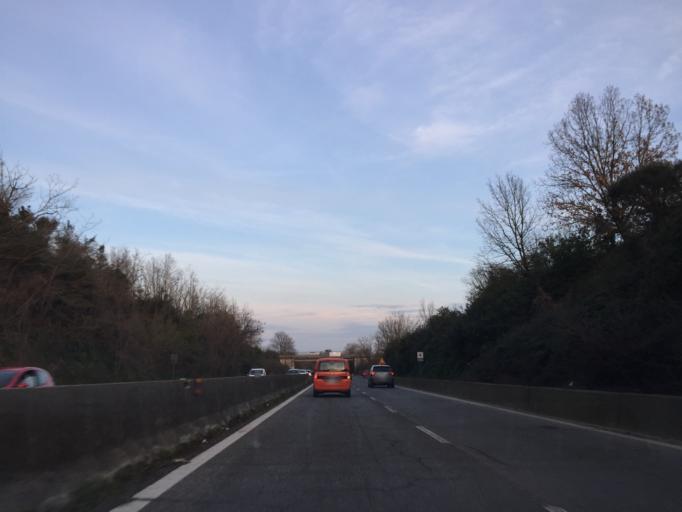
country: IT
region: Latium
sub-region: Citta metropolitana di Roma Capitale
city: Formello
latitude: 42.0440
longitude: 12.4099
